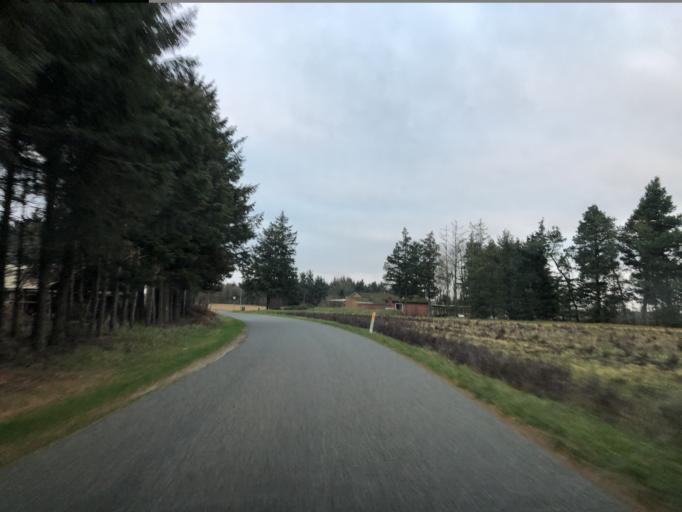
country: DK
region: Central Jutland
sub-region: Holstebro Kommune
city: Ulfborg
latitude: 56.2440
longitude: 8.2885
